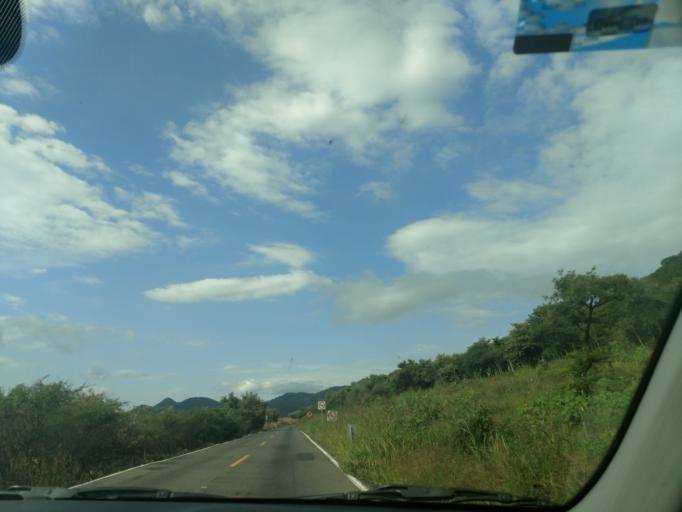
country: MX
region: Jalisco
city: Ameca
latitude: 20.5322
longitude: -104.2040
